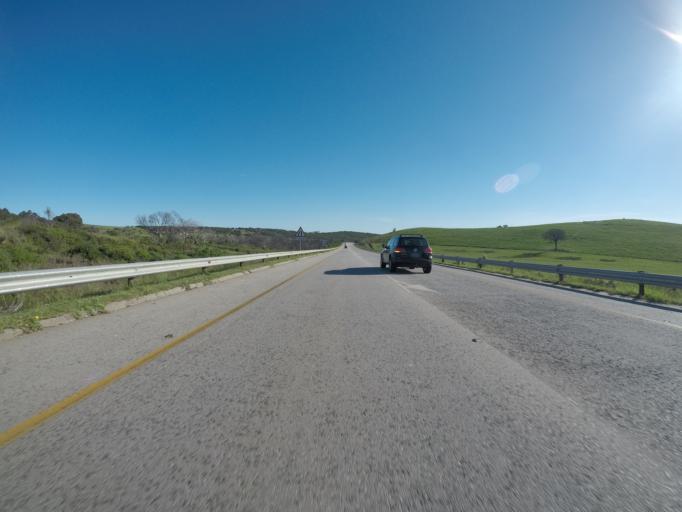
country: ZA
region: Eastern Cape
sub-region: Cacadu District Municipality
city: Jeffrey's Bay
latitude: -33.9005
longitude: 25.1150
